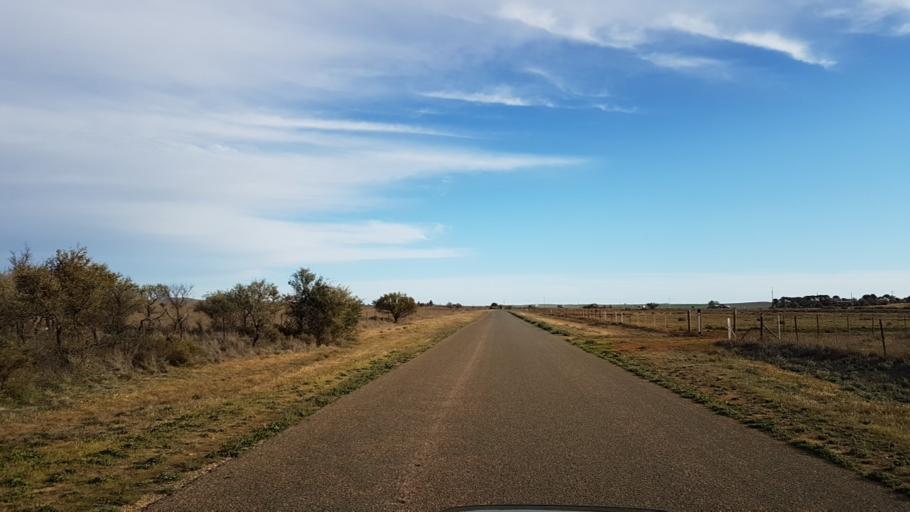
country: AU
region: South Australia
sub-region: Peterborough
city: Peterborough
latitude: -32.9872
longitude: 138.8500
